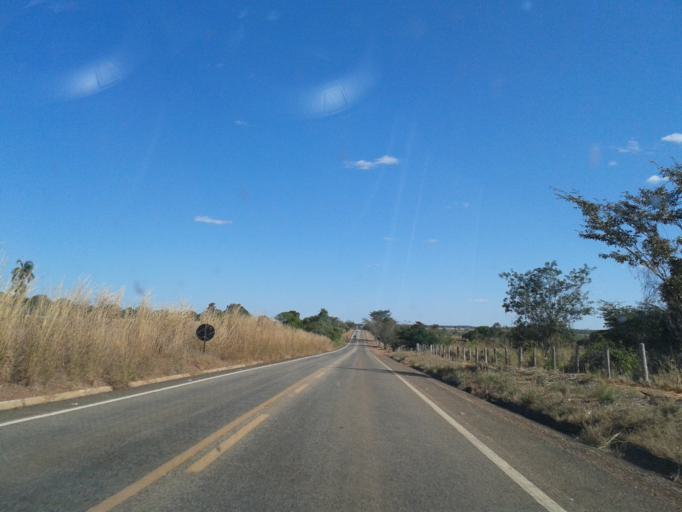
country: BR
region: Goias
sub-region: Mozarlandia
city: Mozarlandia
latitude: -14.5583
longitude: -50.4963
